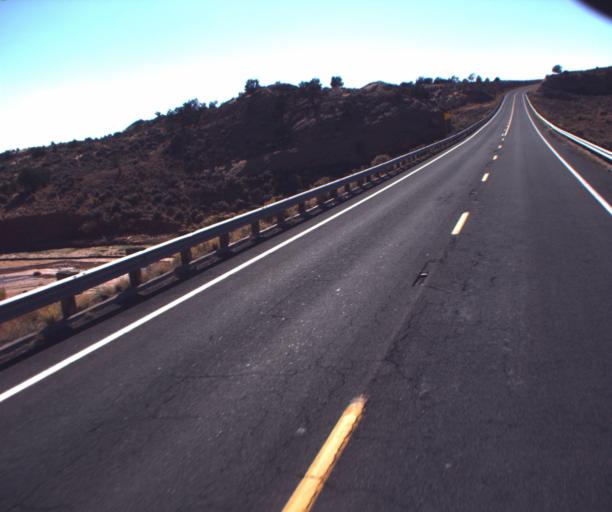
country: US
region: Arizona
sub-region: Coconino County
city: Kaibito
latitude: 36.5617
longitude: -110.7427
